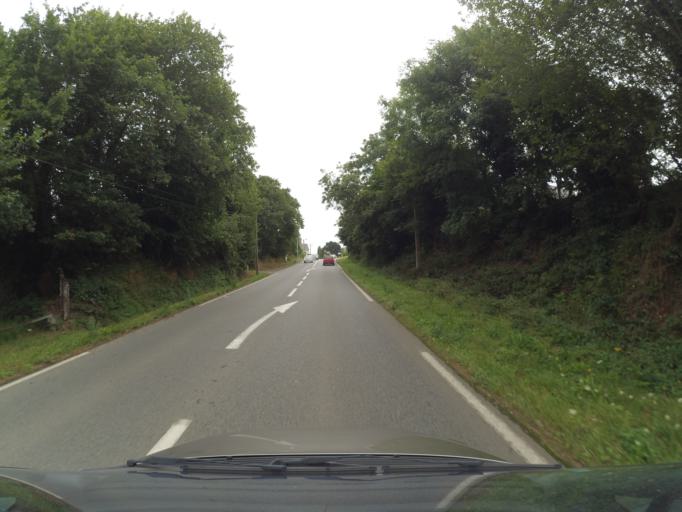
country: FR
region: Brittany
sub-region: Departement des Cotes-d'Armor
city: Ploufragan
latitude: 48.5179
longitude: -2.8074
